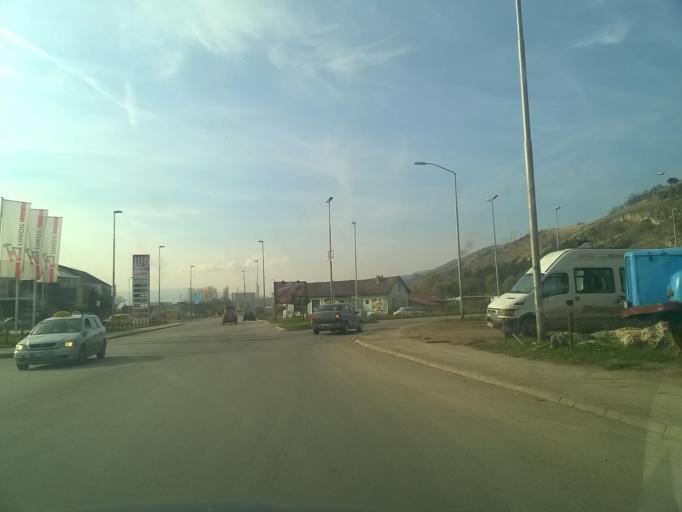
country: RS
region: Central Serbia
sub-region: Pirotski Okrug
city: Pirot
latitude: 43.1580
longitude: 22.5805
